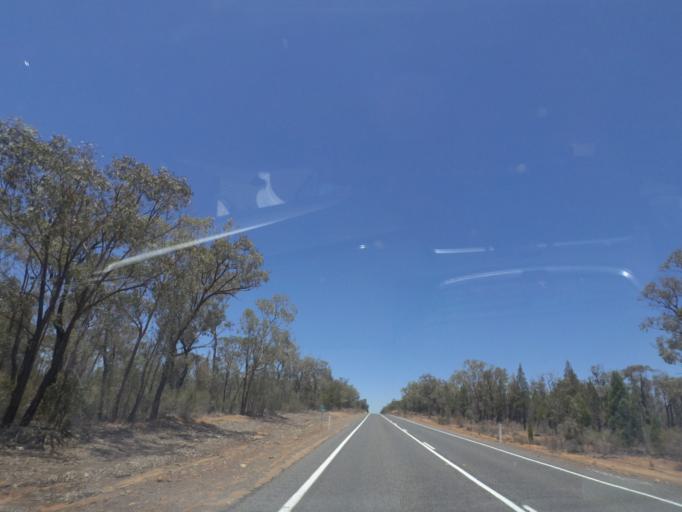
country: AU
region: New South Wales
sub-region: Narrabri
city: Narrabri
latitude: -30.7011
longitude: 149.5345
